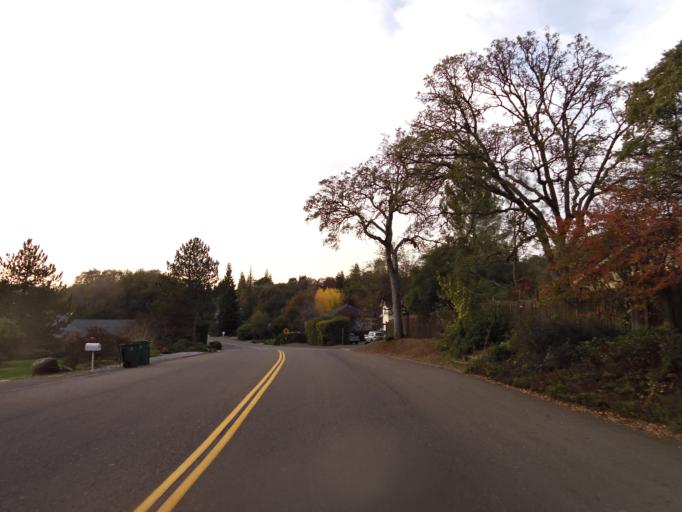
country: US
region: California
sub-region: El Dorado County
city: Cameron Park
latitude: 38.7023
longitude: -120.9976
